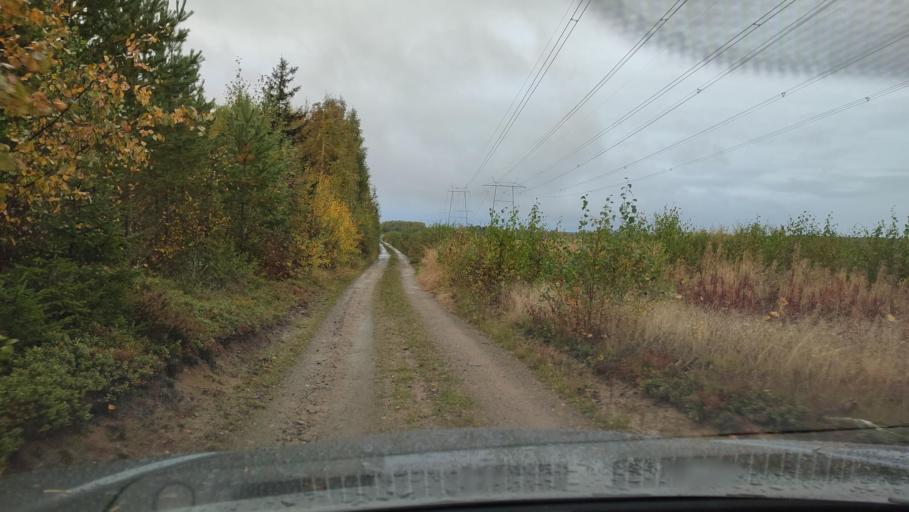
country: FI
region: Southern Ostrobothnia
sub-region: Suupohja
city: Karijoki
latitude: 62.2207
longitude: 21.6286
